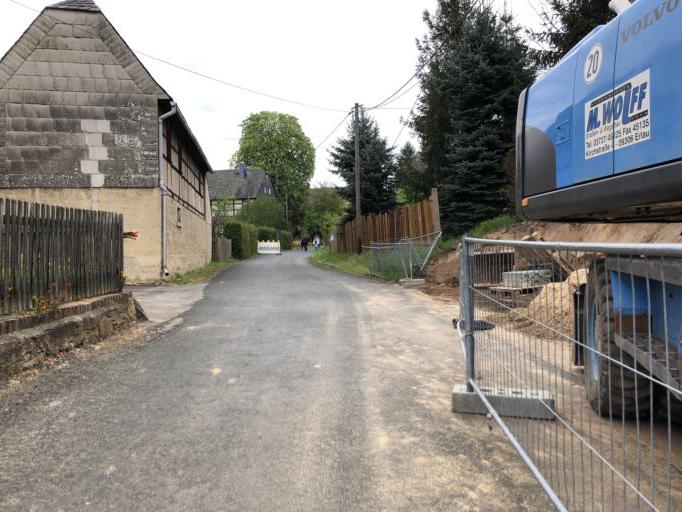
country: DE
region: Saxony
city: Wechselburg
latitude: 51.0197
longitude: 12.7887
